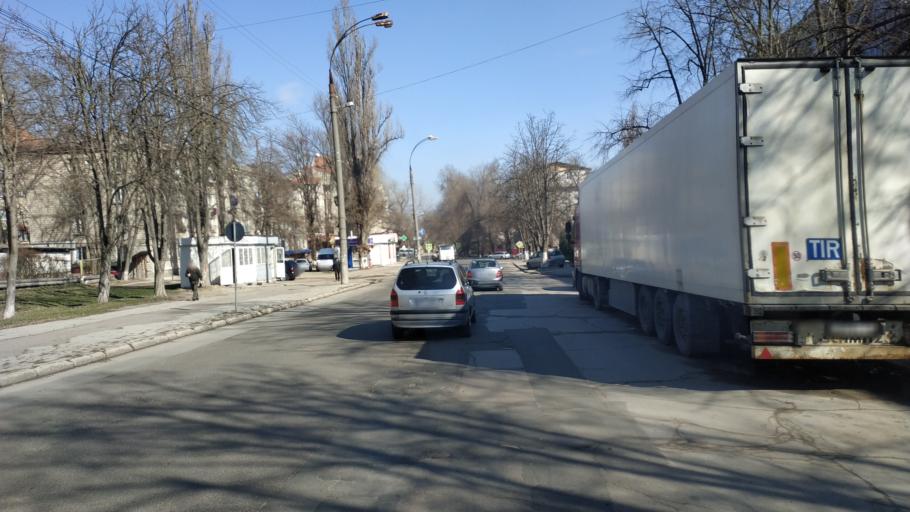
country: MD
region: Chisinau
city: Vatra
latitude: 47.0315
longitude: 28.7911
